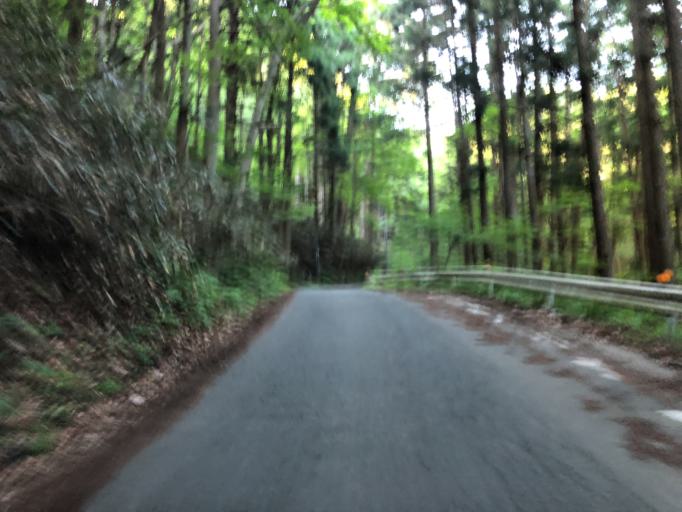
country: JP
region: Ibaraki
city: Kitaibaraki
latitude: 36.8901
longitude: 140.6224
